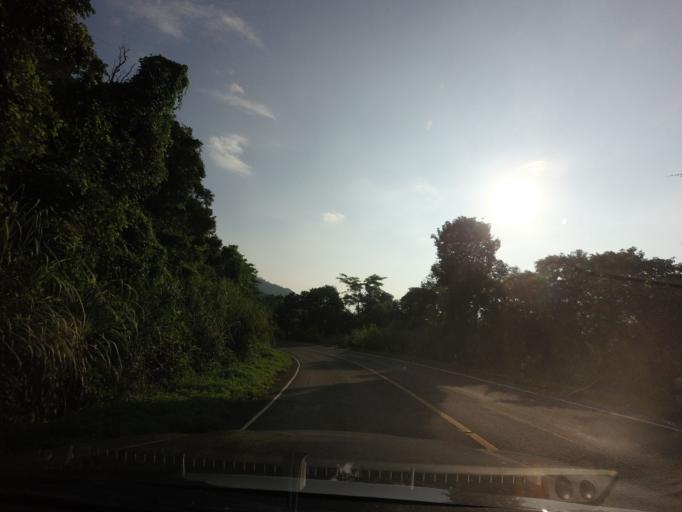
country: TH
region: Nan
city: Na Noi
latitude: 18.3665
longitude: 100.8276
